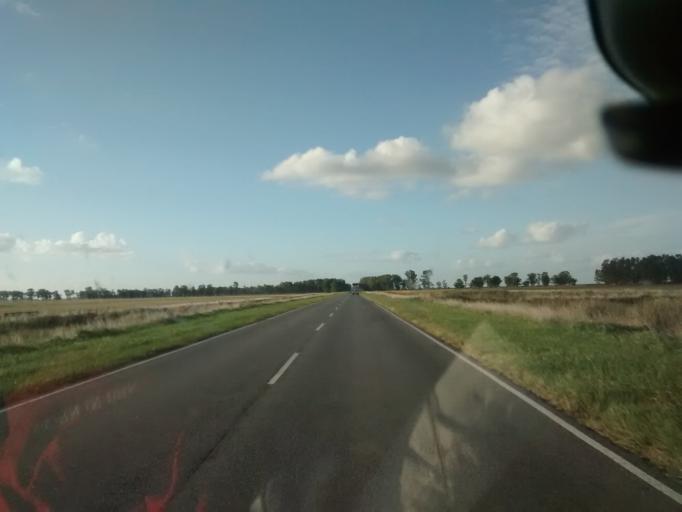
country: AR
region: Buenos Aires
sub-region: Partido de General Belgrano
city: General Belgrano
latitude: -36.1631
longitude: -58.5946
